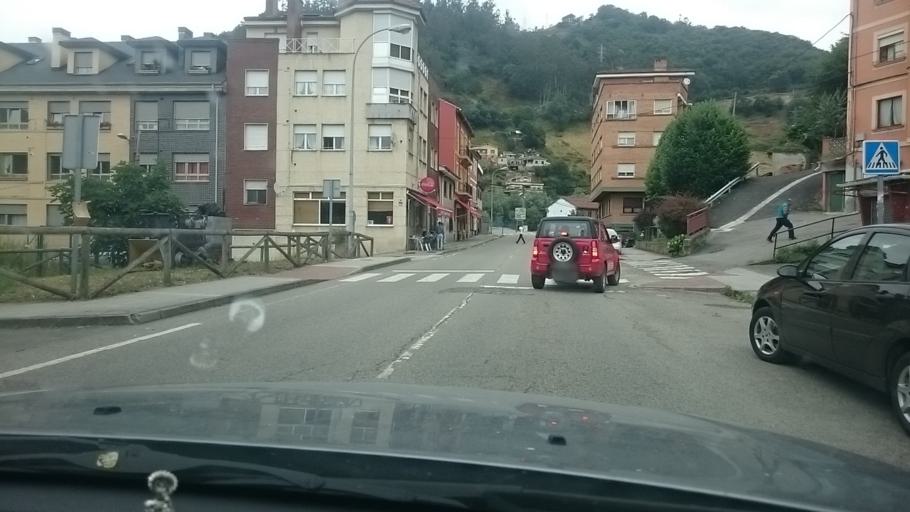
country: ES
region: Asturias
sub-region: Province of Asturias
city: Mieres
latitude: 43.2098
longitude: -5.7832
